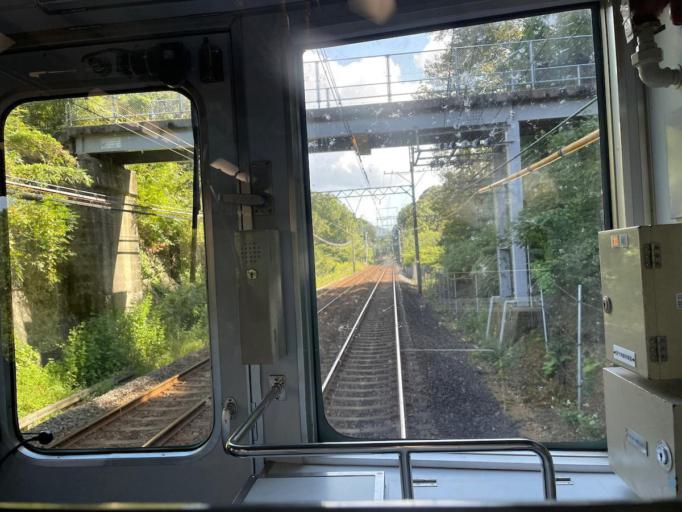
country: JP
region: Mie
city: Ise
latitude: 34.4746
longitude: 136.7479
